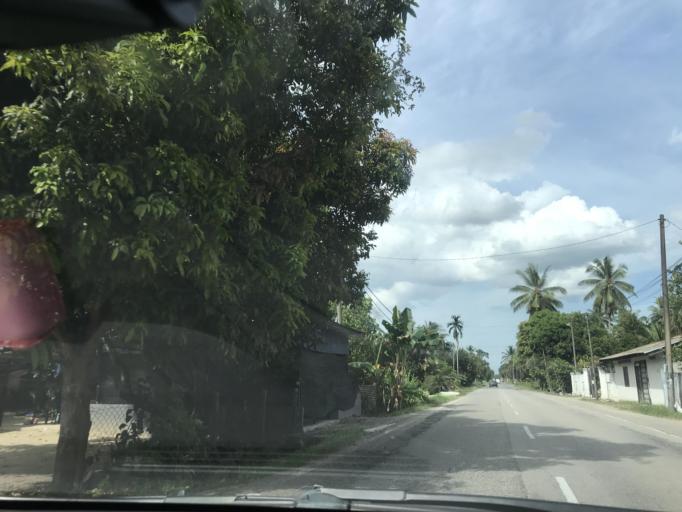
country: MY
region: Kelantan
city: Kampung Lemal
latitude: 6.0339
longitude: 102.1695
